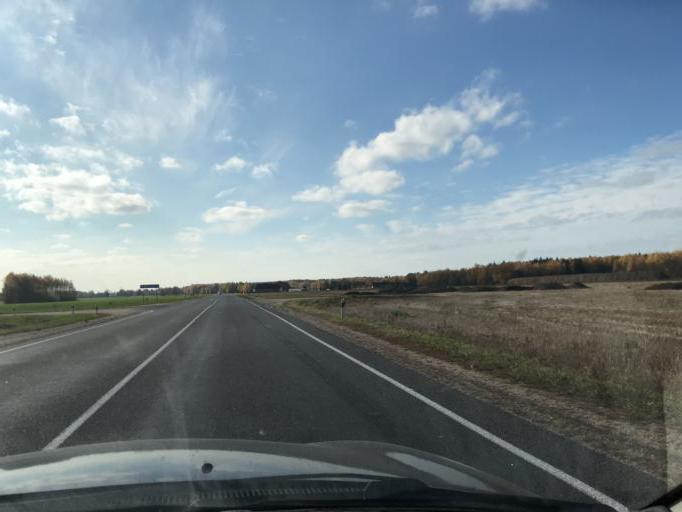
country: BY
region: Grodnenskaya
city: Voranava
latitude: 54.1908
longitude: 25.3439
